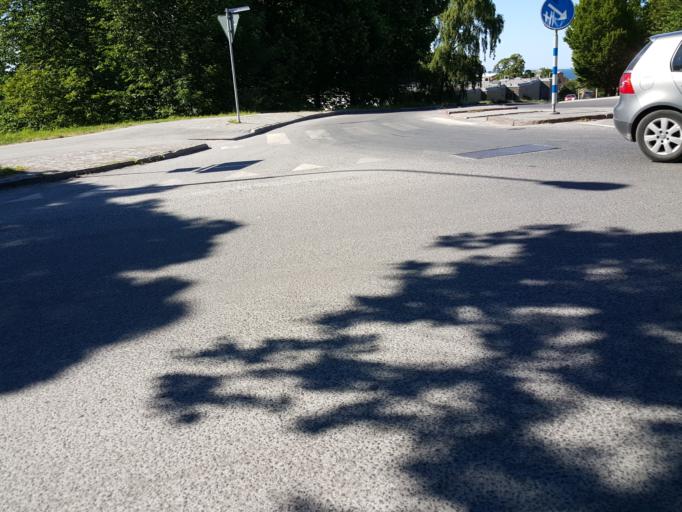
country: SE
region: Gotland
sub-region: Gotland
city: Visby
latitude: 57.6449
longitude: 18.3018
